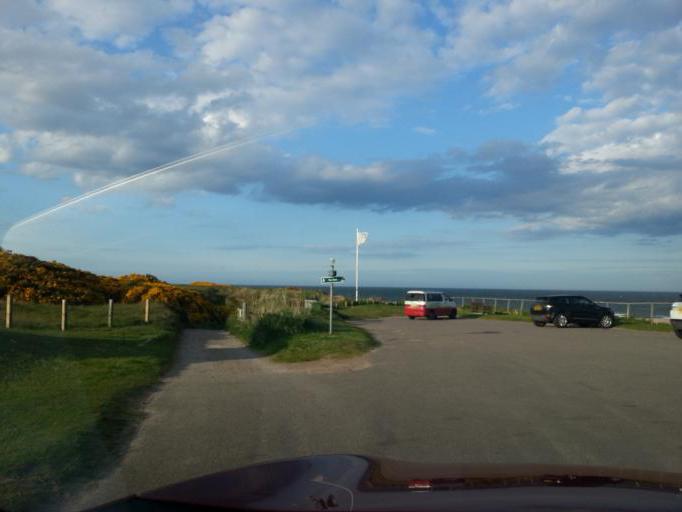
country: GB
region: Scotland
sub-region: Highland
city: Dornoch
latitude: 57.8791
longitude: -4.0157
